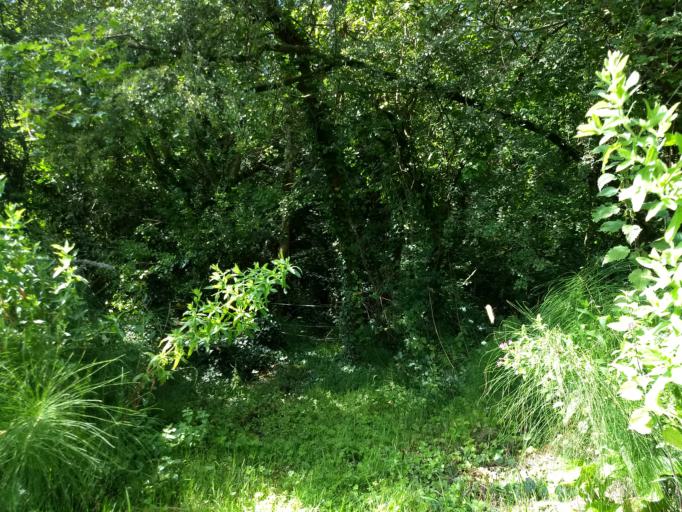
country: GB
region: England
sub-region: Isle of Wight
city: Ryde
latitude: 50.7083
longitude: -1.1493
